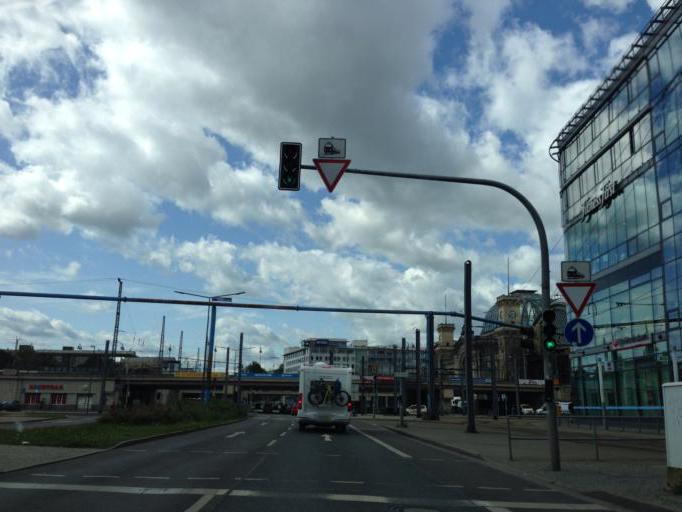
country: DE
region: Saxony
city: Dresden
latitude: 51.0414
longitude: 13.7351
